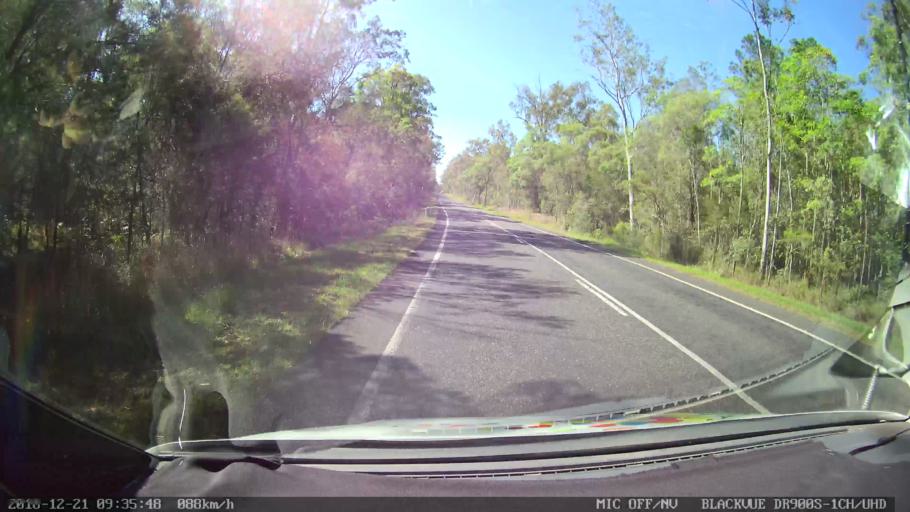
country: AU
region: New South Wales
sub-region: Clarence Valley
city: Grafton
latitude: -29.5153
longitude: 152.9804
